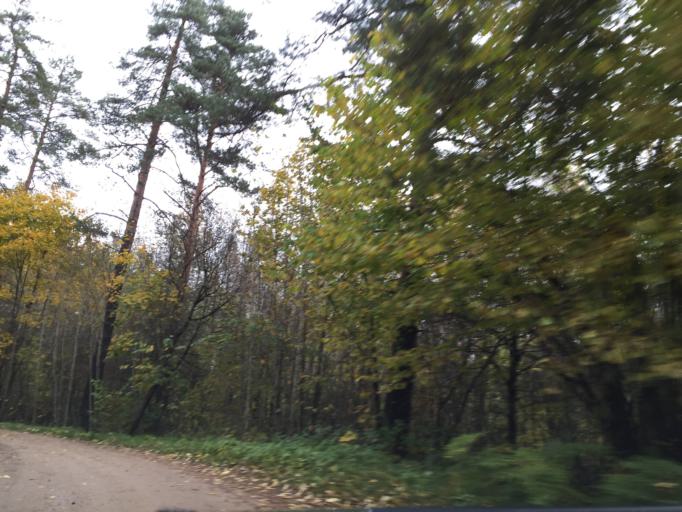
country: LV
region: Ogre
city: Ogre
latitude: 56.8021
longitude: 24.6378
